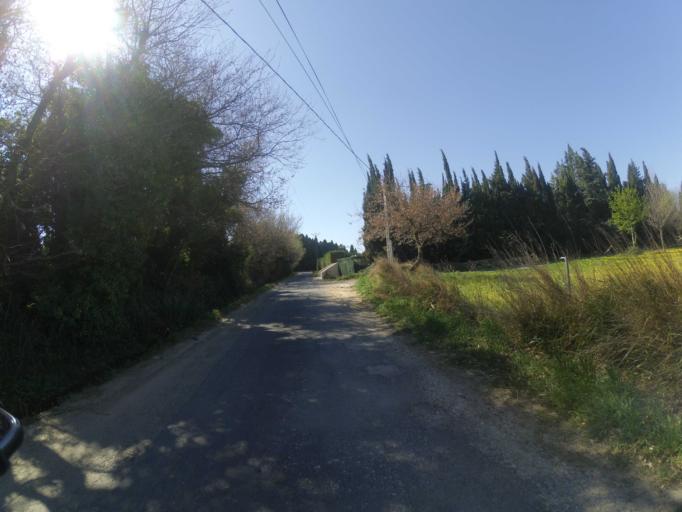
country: FR
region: Languedoc-Roussillon
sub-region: Departement des Pyrenees-Orientales
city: Pezilla-la-Riviere
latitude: 42.7033
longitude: 2.7736
